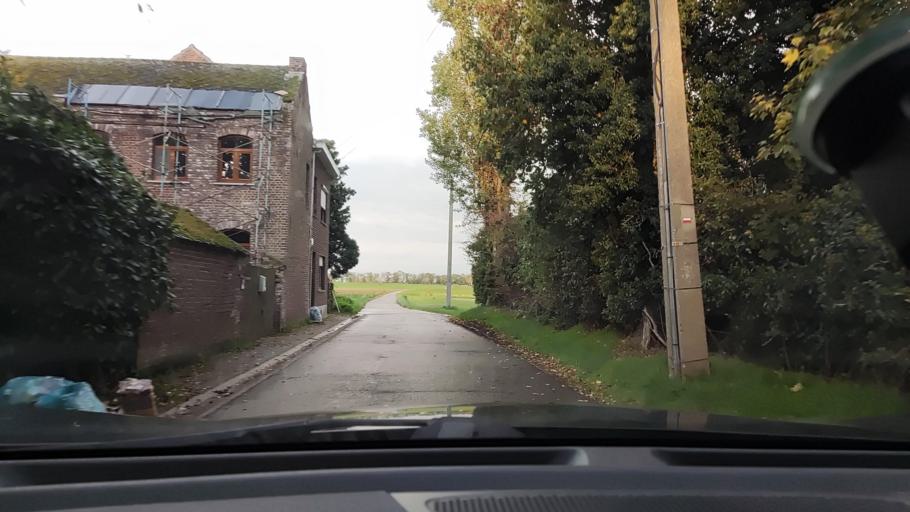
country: BE
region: Flanders
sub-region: Provincie Vlaams-Brabant
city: Tienen
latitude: 50.7725
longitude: 4.9424
